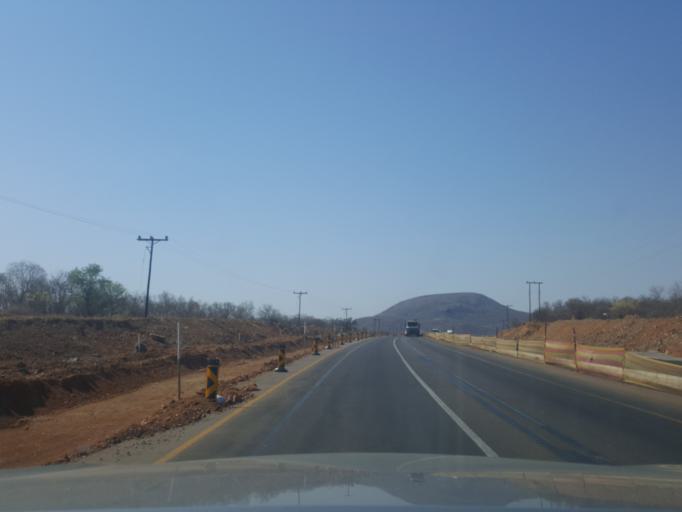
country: BW
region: Kweneng
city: Gabane
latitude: -24.7488
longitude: 25.8290
